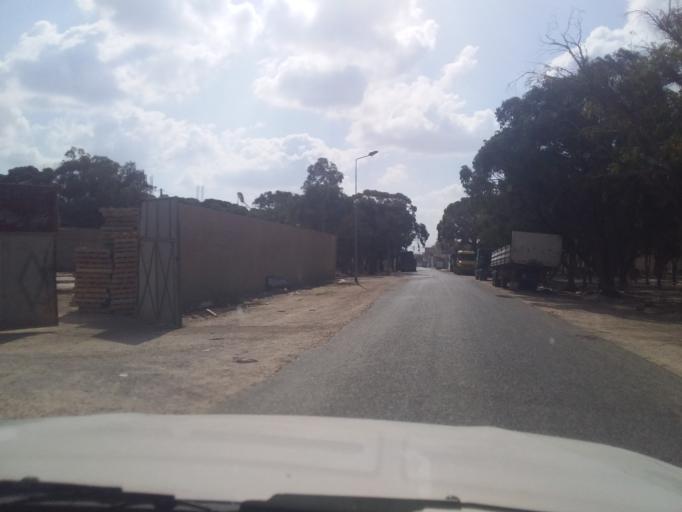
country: TN
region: Qabis
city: Gabes
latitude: 33.6229
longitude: 10.2785
